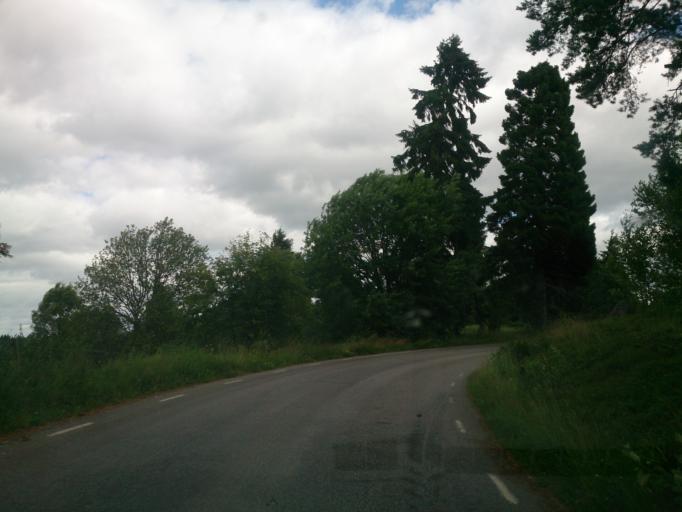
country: SE
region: OEstergoetland
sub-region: Norrkopings Kommun
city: Krokek
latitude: 58.5069
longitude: 16.5914
